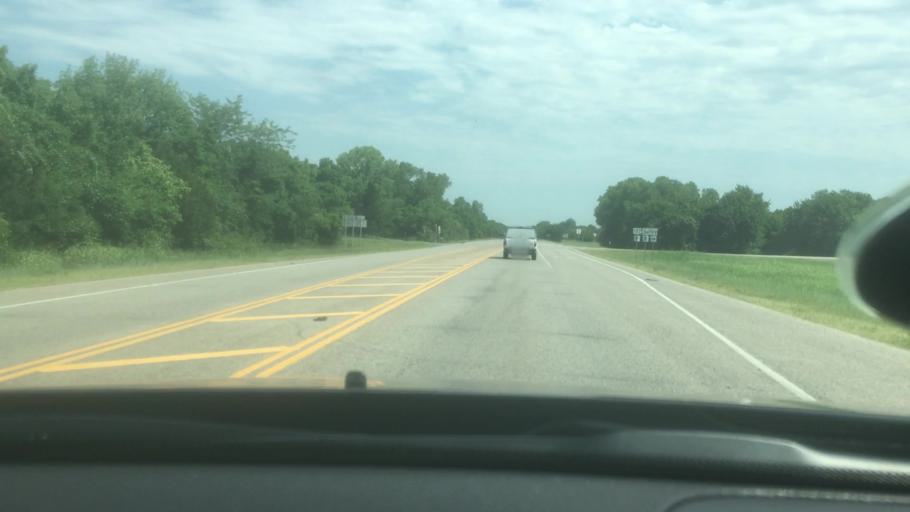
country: US
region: Oklahoma
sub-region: Seminole County
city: Maud
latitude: 35.0716
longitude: -96.9312
